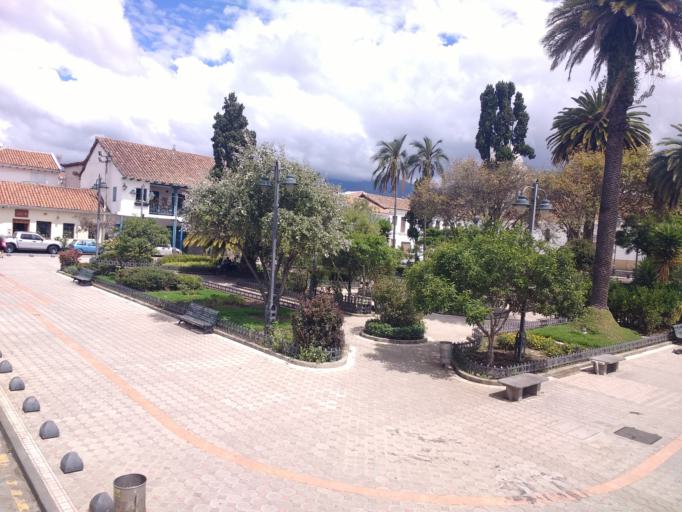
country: EC
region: Azuay
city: Cuenca
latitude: -2.8962
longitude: -79.0110
